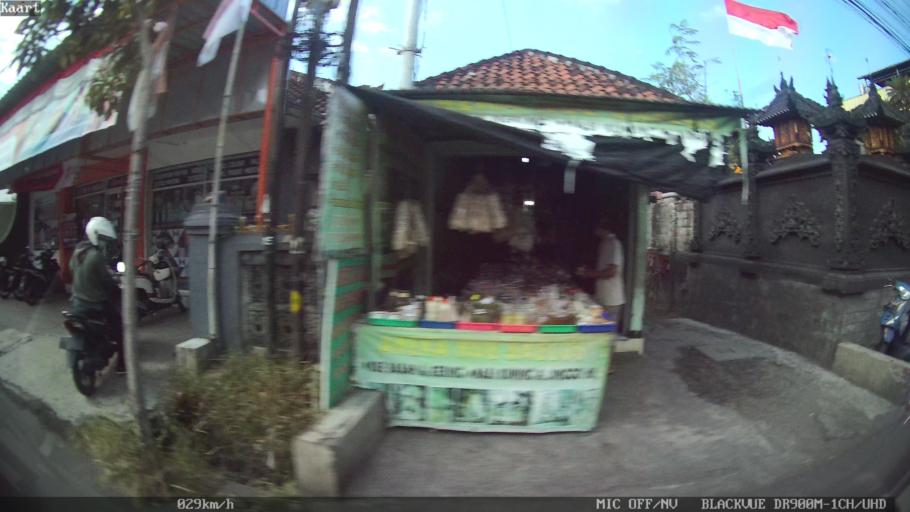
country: ID
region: Bali
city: Karyadharma
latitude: -8.6848
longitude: 115.2147
